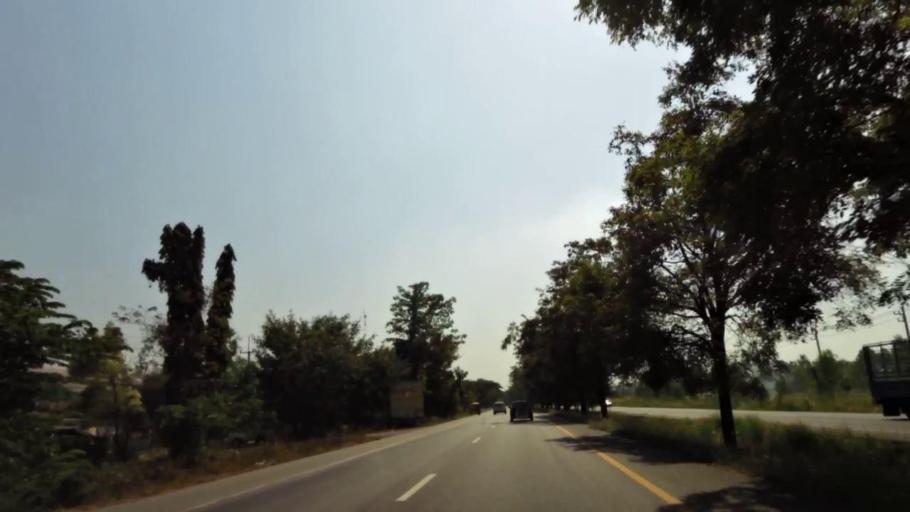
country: TH
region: Phichit
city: Bueng Na Rang
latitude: 16.0201
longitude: 100.1145
